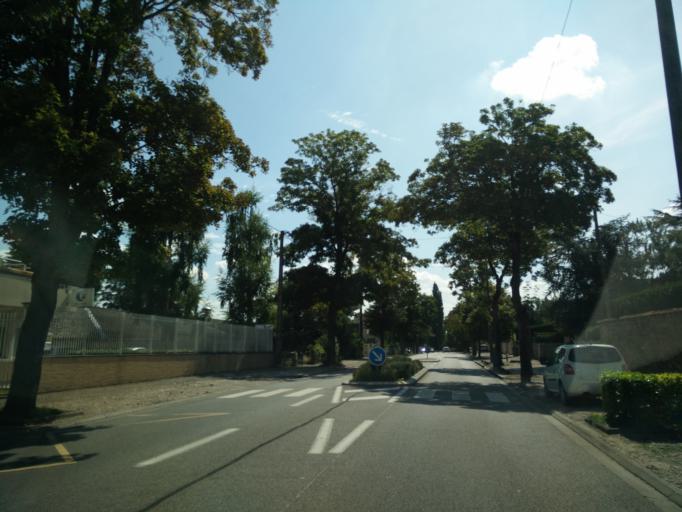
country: FR
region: Haute-Normandie
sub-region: Departement de l'Eure
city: Vernon
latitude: 49.0847
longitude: 1.4992
